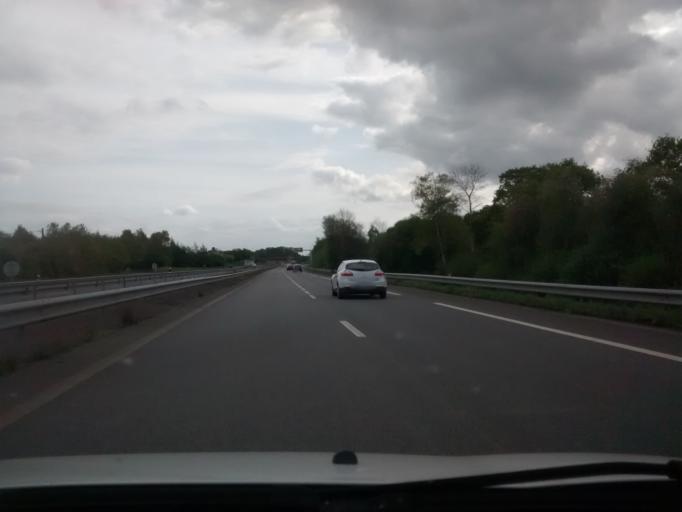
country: FR
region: Brittany
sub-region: Departement d'Ille-et-Vilaine
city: Saint-Pierre-de-Plesguen
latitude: 48.4643
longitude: -1.9147
